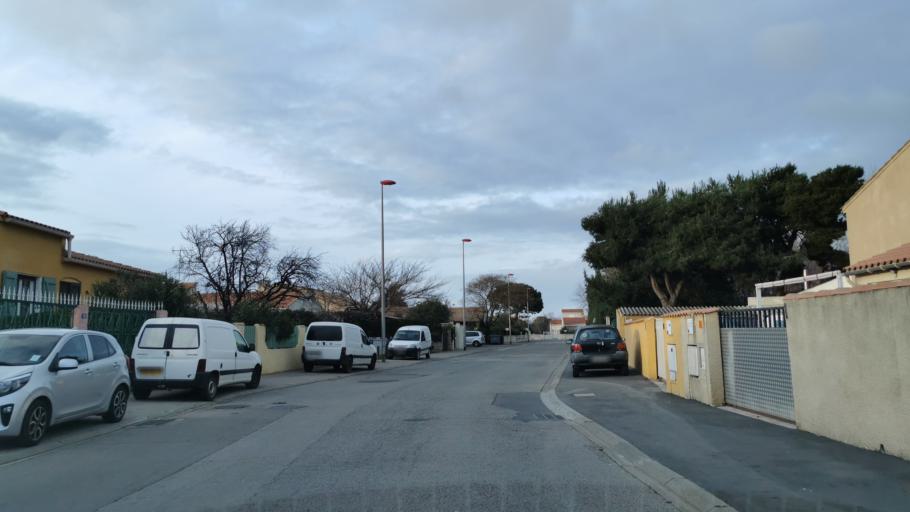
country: FR
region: Languedoc-Roussillon
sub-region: Departement de l'Aude
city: Narbonne
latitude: 43.1862
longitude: 2.9794
